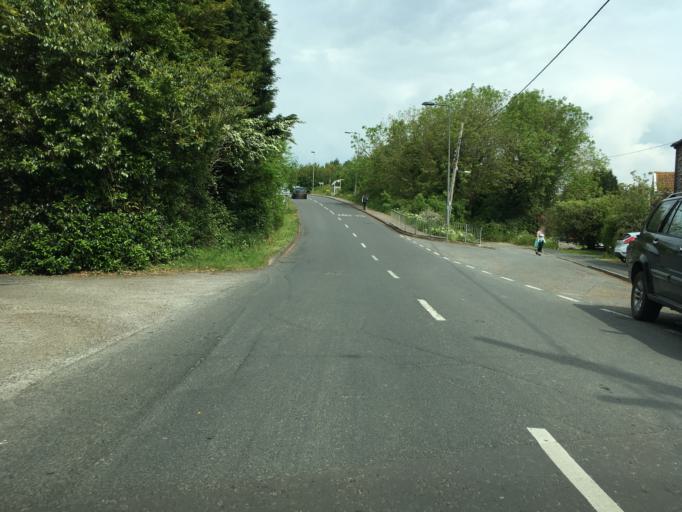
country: GB
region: England
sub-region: South Gloucestershire
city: Severn Beach
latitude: 51.5675
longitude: -2.6498
